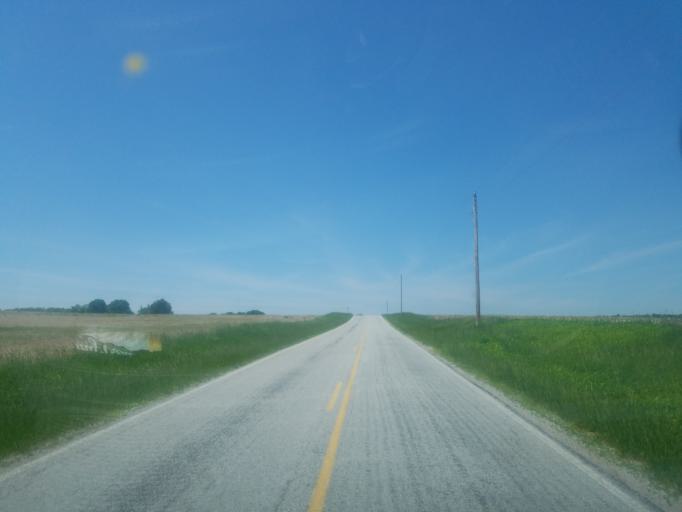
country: US
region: Ohio
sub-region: Huron County
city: New London
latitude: 41.1109
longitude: -82.4577
